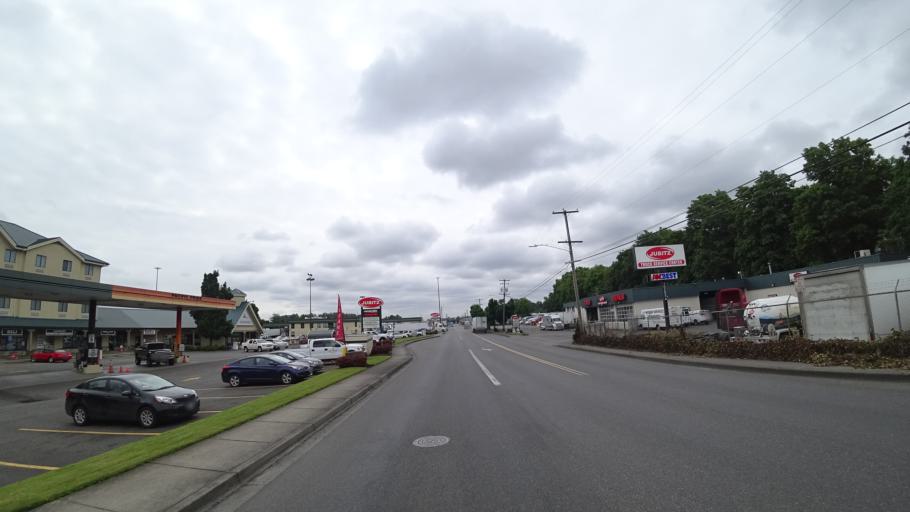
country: US
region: Washington
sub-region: Clark County
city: Vancouver
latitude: 45.5973
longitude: -122.6705
